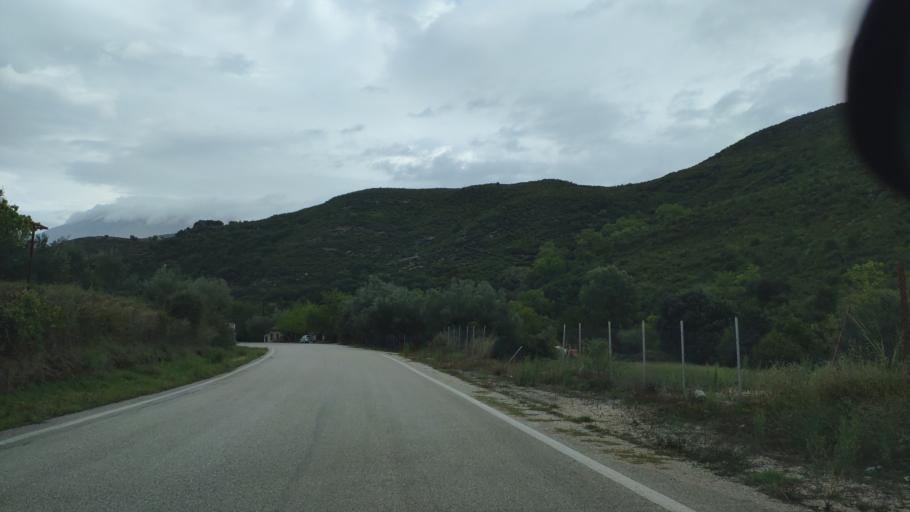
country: GR
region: West Greece
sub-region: Nomos Aitolias kai Akarnanias
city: Sardinia
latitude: 38.9140
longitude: 21.3569
